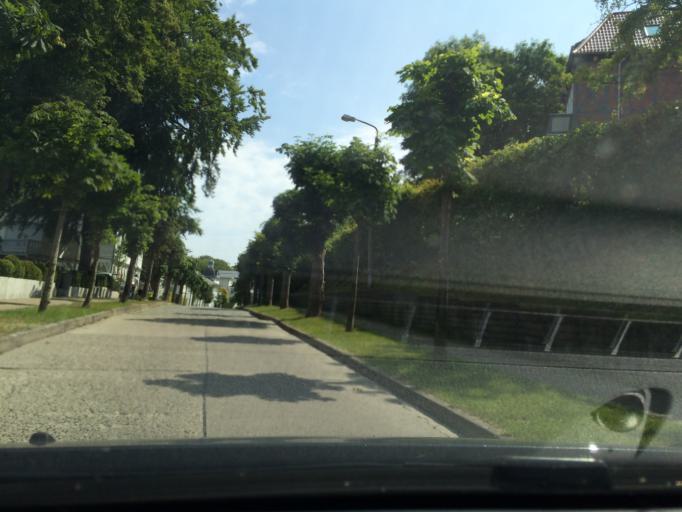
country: DE
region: Mecklenburg-Vorpommern
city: Ostseebad Binz
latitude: 54.3989
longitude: 13.6119
